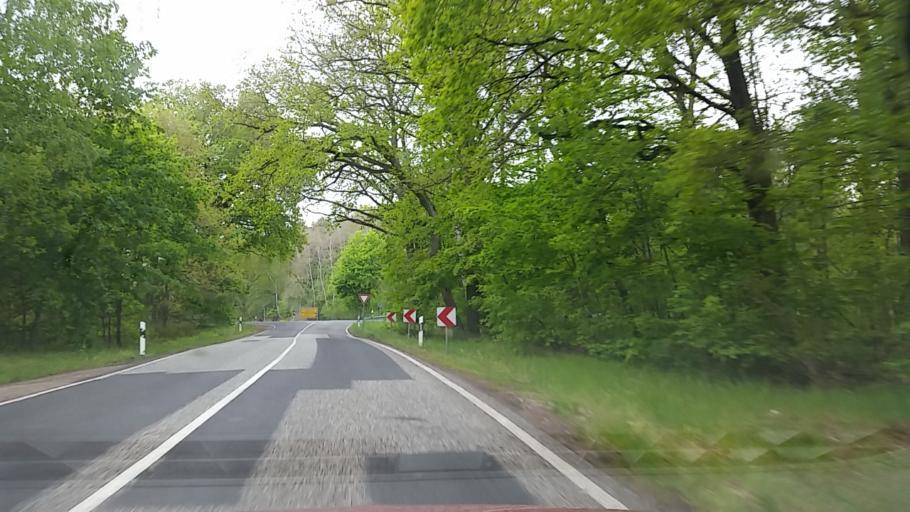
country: DE
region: Brandenburg
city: Spreenhagen
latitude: 52.3214
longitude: 13.9038
